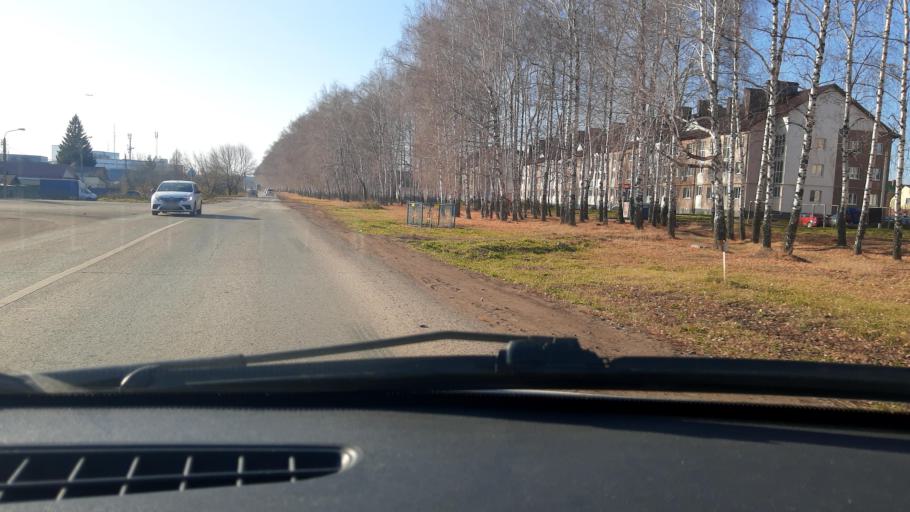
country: RU
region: Bashkortostan
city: Avdon
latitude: 54.6941
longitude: 55.8033
